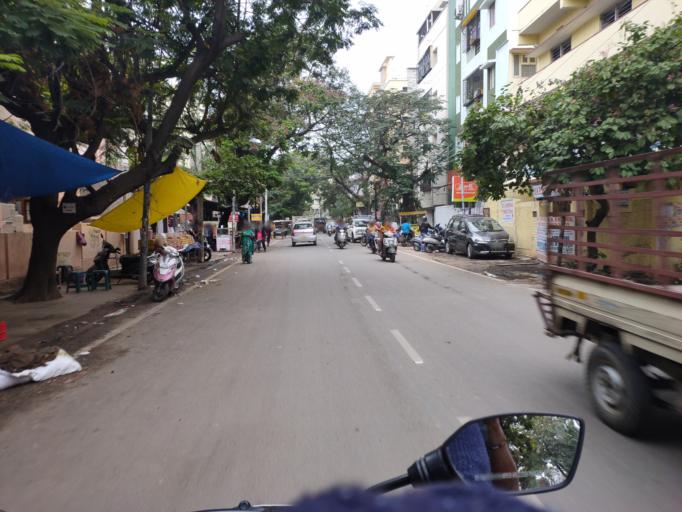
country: IN
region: Telangana
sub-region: Rangareddi
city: Kukatpalli
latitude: 17.4458
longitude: 78.4469
